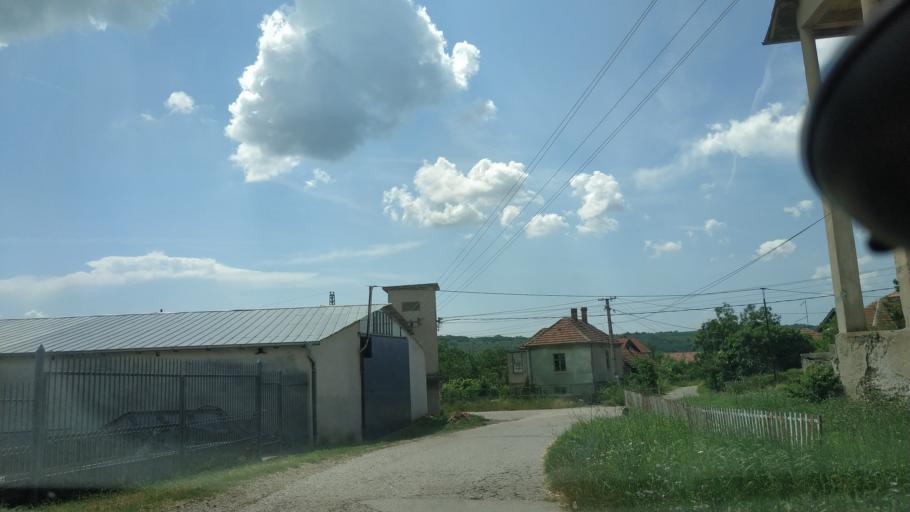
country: RS
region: Central Serbia
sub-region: Nisavski Okrug
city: Aleksinac
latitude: 43.5987
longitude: 21.6936
